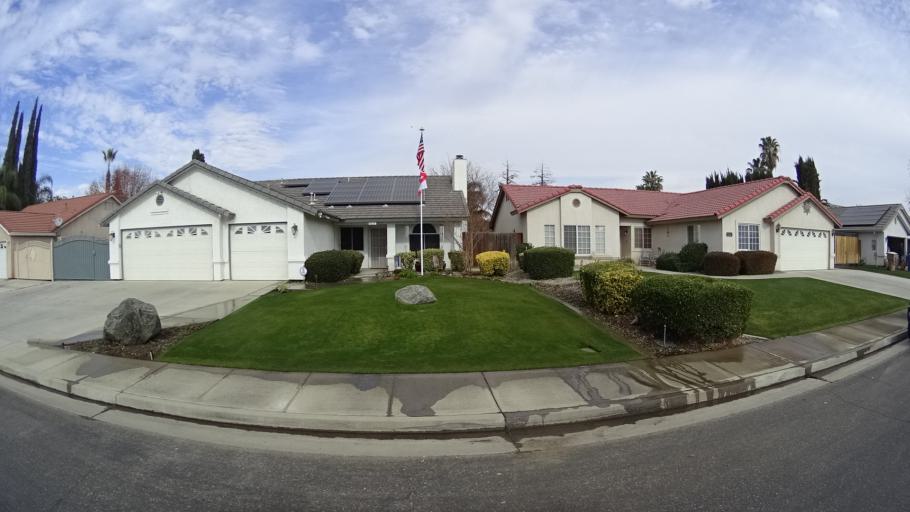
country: US
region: California
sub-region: Kern County
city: Rosedale
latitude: 35.3961
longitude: -119.1350
